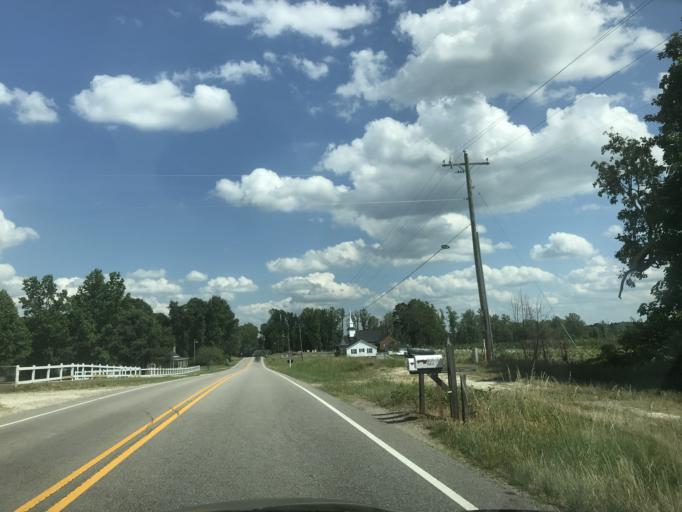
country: US
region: North Carolina
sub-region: Wake County
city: Rolesville
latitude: 35.9733
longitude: -78.3437
